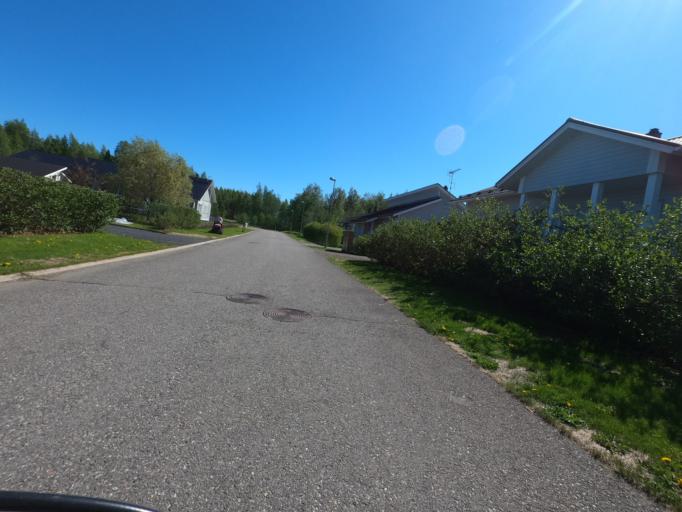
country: FI
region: North Karelia
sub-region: Joensuu
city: Joensuu
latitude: 62.6038
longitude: 29.8249
